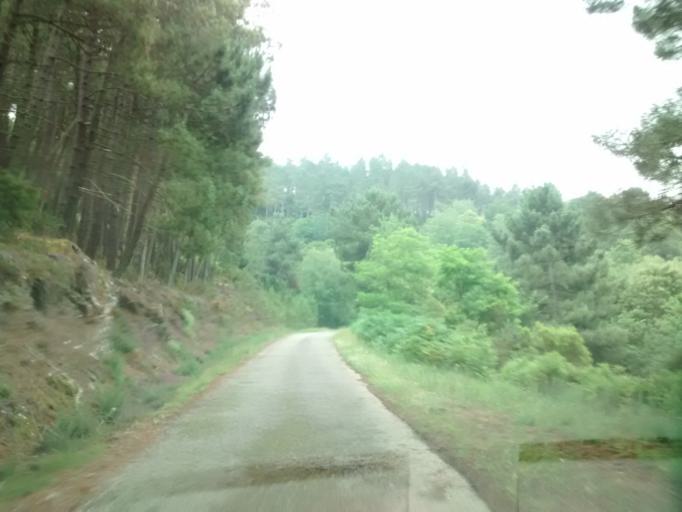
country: ES
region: Galicia
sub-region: Provincia de Ourense
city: Castro Caldelas
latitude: 42.4159
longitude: -7.3878
